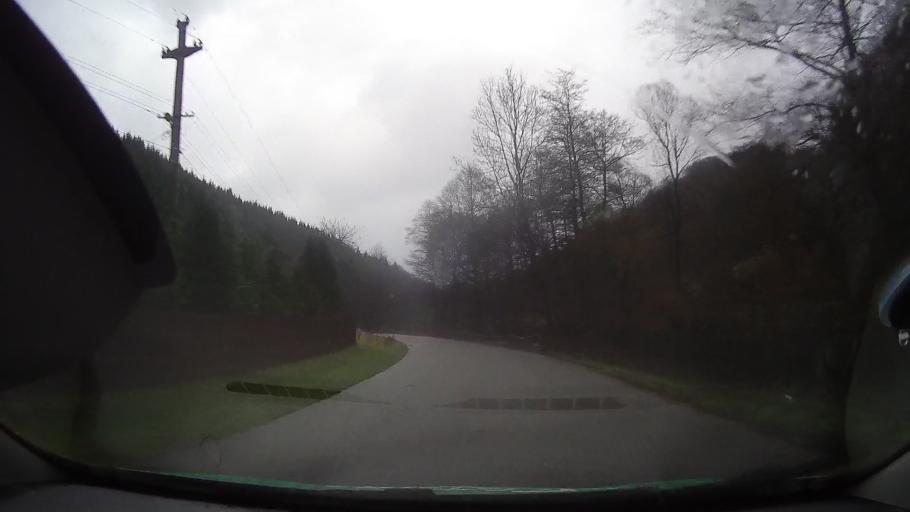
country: RO
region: Alba
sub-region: Comuna Avram Iancu
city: Avram Iancu
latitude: 46.2920
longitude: 22.7538
